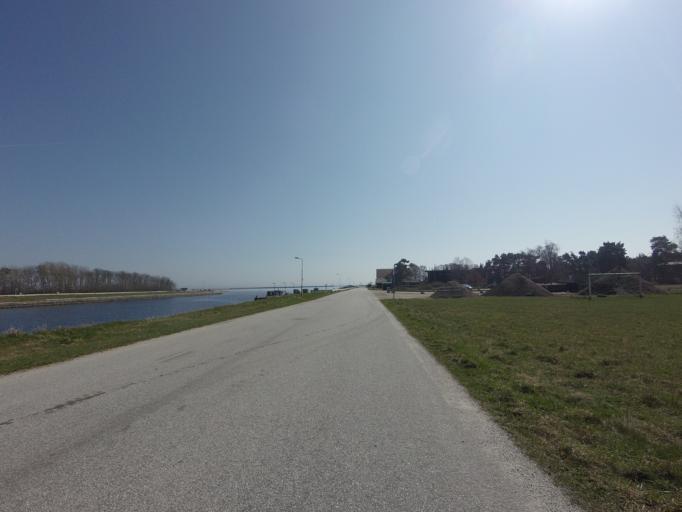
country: SE
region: Skane
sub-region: Vellinge Kommun
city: Hollviken
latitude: 55.3994
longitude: 12.9428
